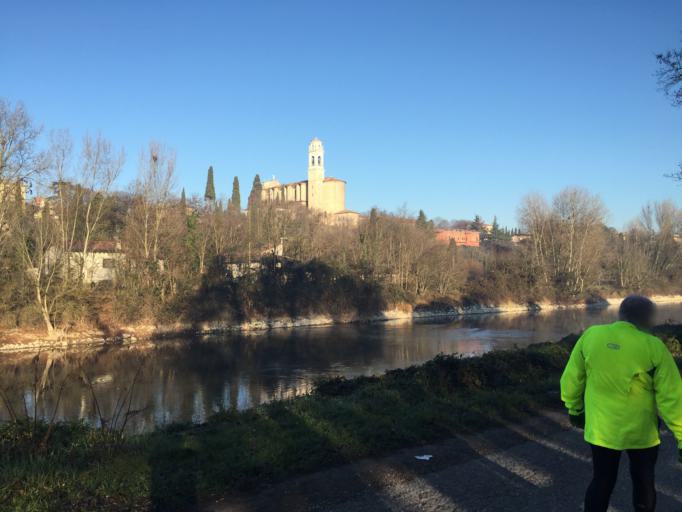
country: IT
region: Lombardy
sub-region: Provincia di Mantova
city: Monzambano
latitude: 45.3851
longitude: 10.6966
